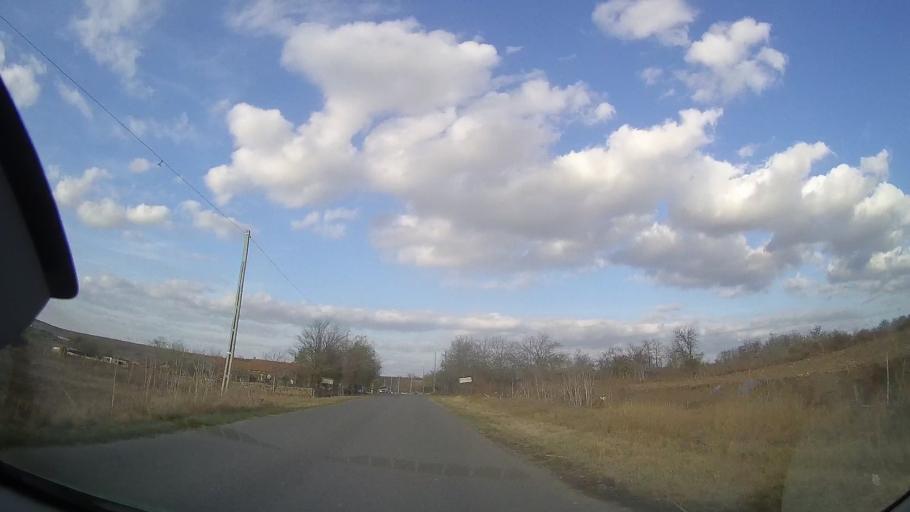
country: RO
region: Constanta
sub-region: Comuna Cerchezu
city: Cerchezu
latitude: 43.8526
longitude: 28.1009
